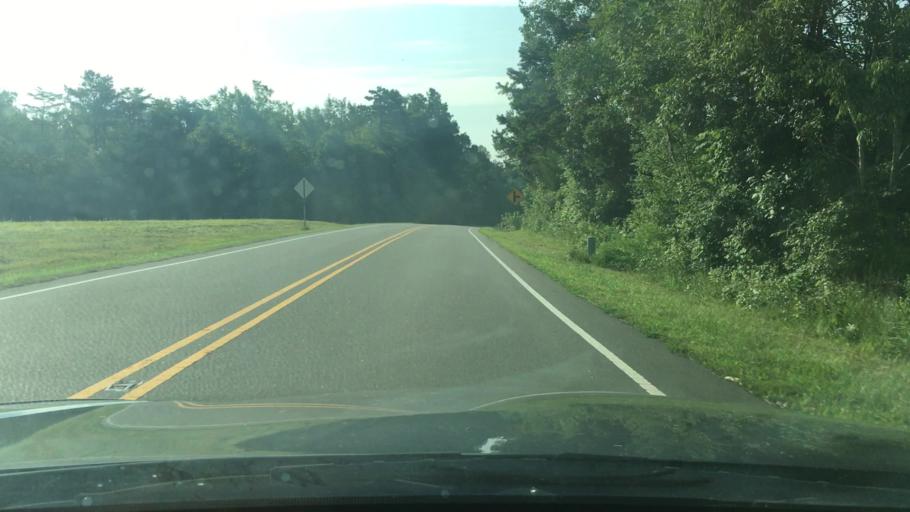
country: US
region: North Carolina
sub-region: Alamance County
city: Green Level
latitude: 36.2566
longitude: -79.3352
